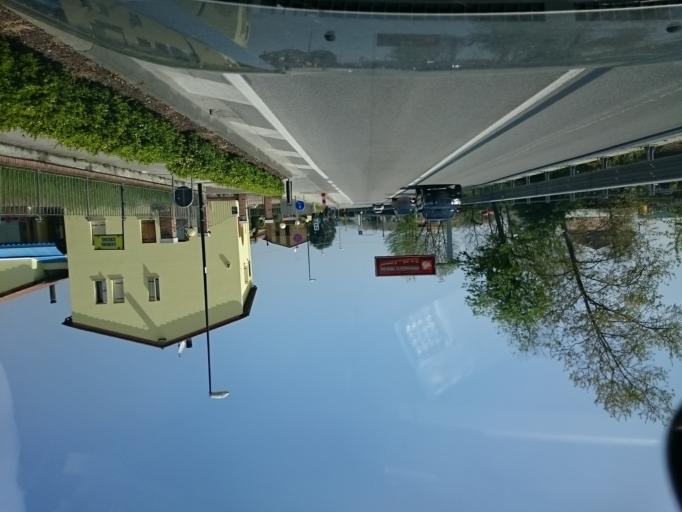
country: IT
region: Veneto
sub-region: Provincia di Vicenza
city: Rossano Veneto
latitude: 45.7011
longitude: 11.8214
